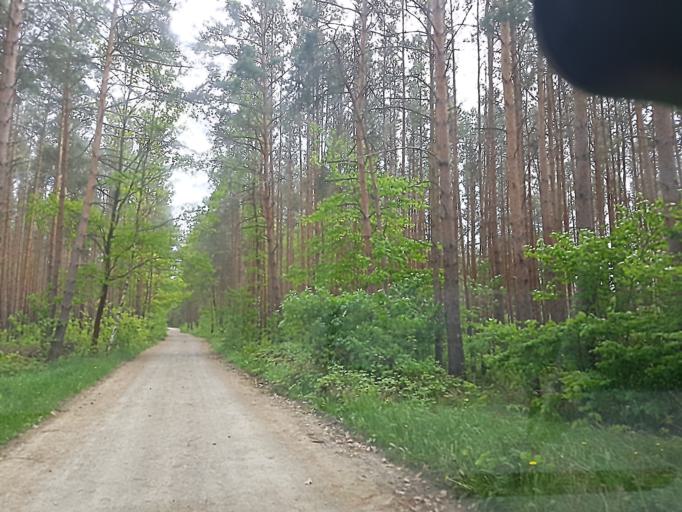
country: DE
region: Brandenburg
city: Finsterwalde
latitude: 51.5862
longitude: 13.7069
